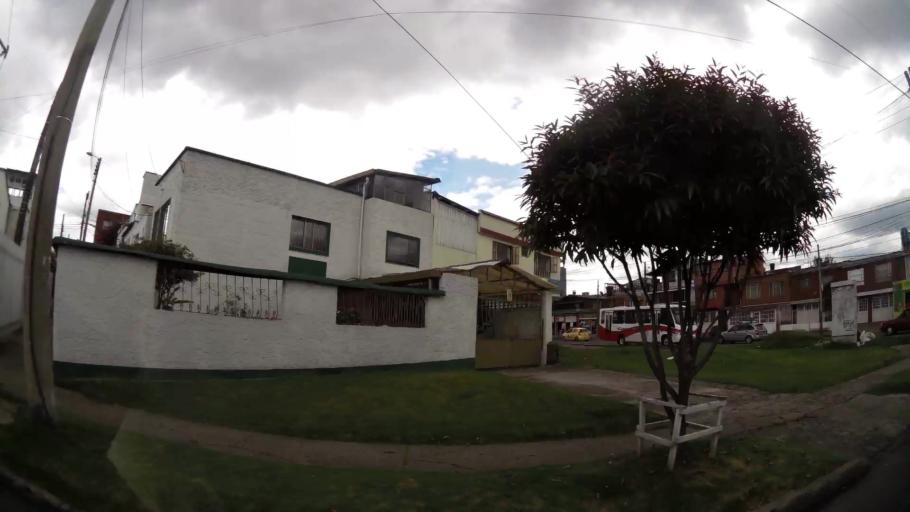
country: CO
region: Bogota D.C.
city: Barrio San Luis
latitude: 4.7045
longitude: -74.0922
